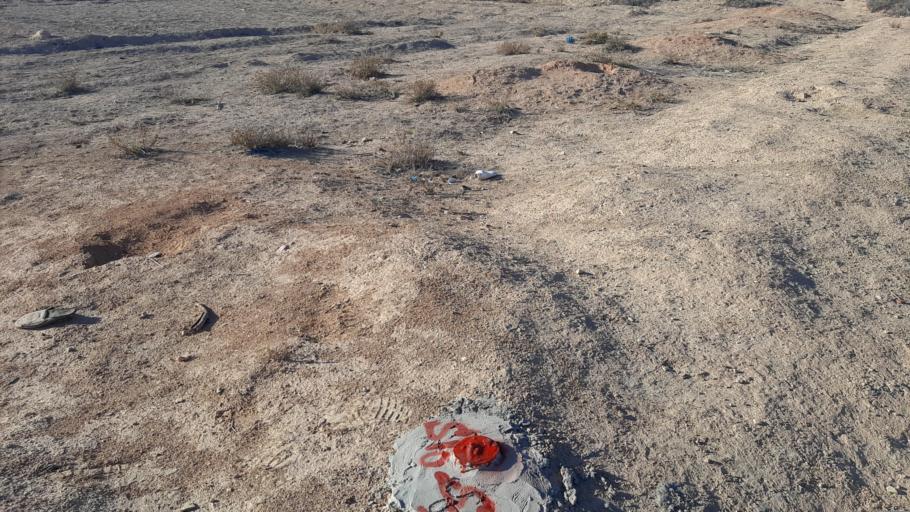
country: TN
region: Qabis
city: Gabes
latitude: 33.8641
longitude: 10.0705
